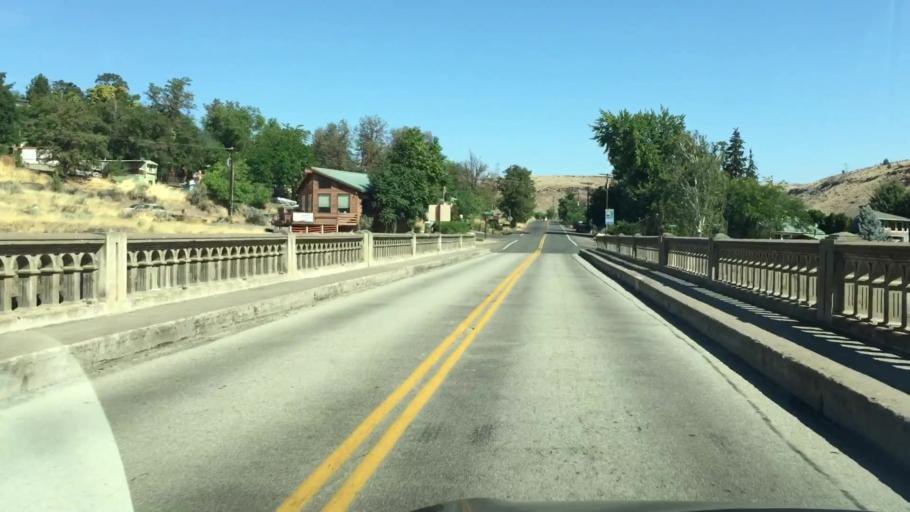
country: US
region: Oregon
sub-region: Wasco County
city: The Dalles
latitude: 45.1729
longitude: -121.0765
